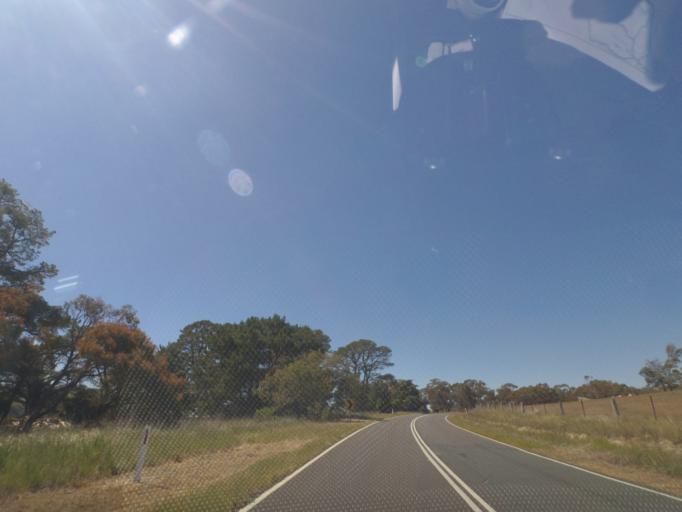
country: AU
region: Victoria
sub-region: Hume
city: Sunbury
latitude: -37.0730
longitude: 144.7720
